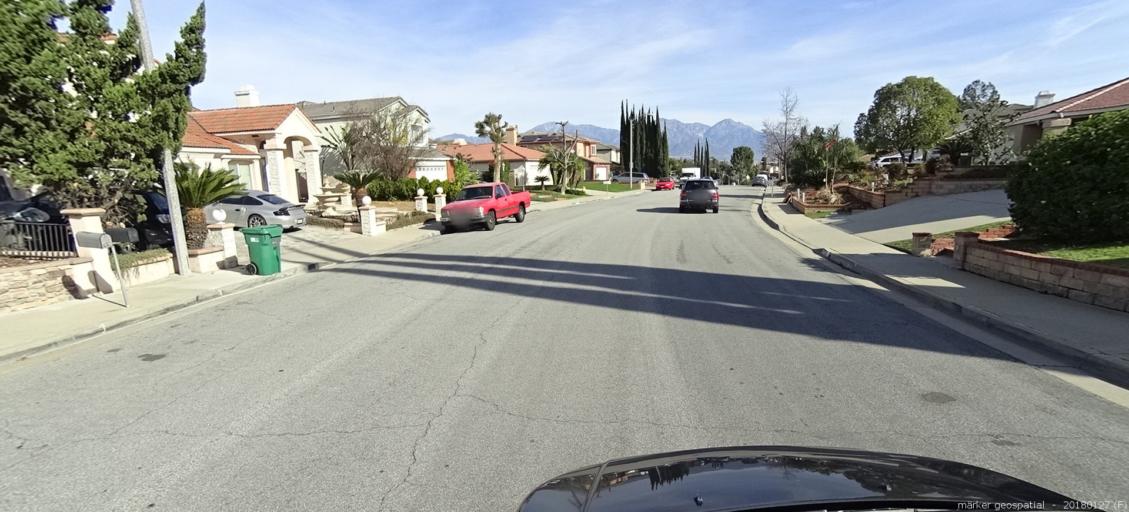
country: US
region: California
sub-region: Los Angeles County
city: Diamond Bar
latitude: 34.0291
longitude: -117.7890
